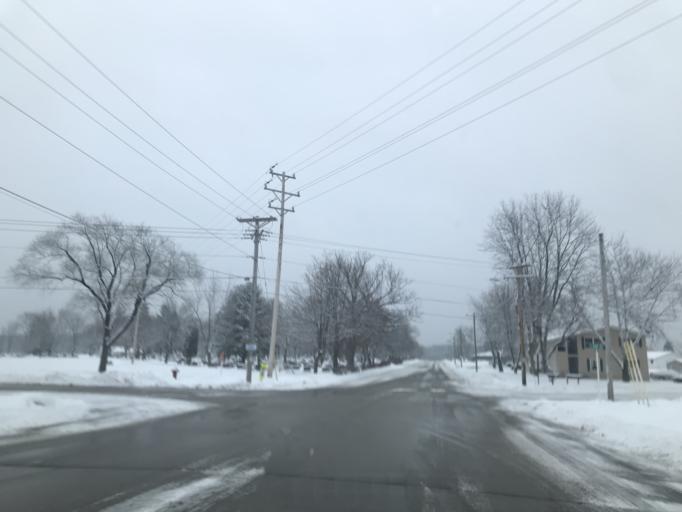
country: US
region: Wisconsin
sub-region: Oconto County
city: Oconto Falls
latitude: 44.8682
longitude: -88.1309
